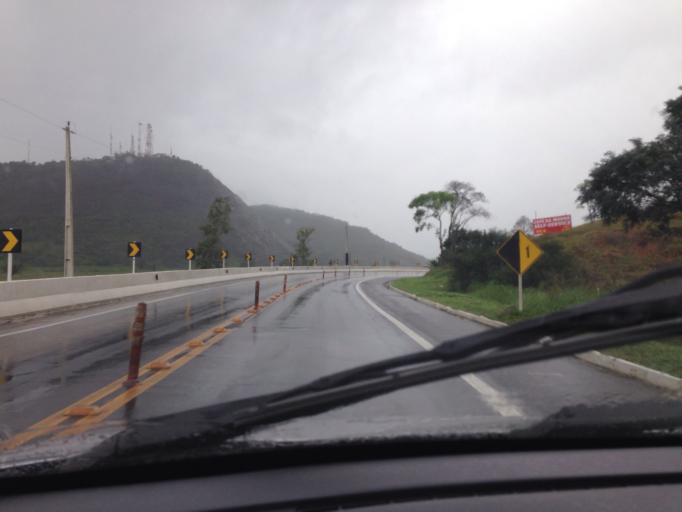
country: BR
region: Espirito Santo
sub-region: Guarapari
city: Guarapari
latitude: -20.6107
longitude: -40.5104
